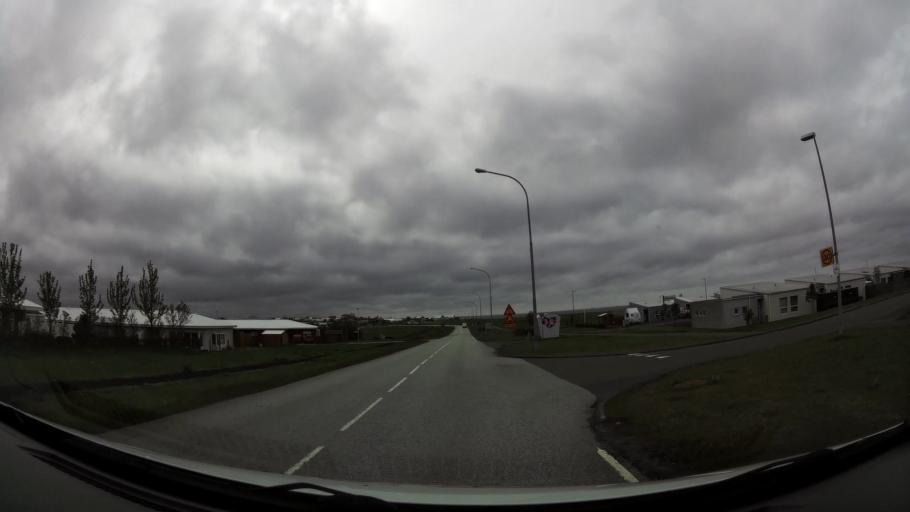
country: IS
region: Capital Region
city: Alftanes
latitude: 64.1085
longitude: -22.0208
